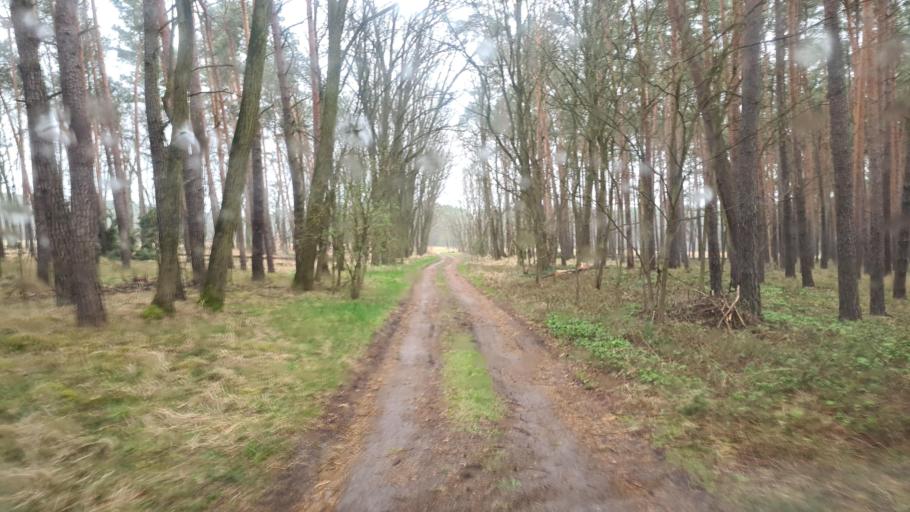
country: DE
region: Brandenburg
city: Bruck
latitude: 52.1626
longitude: 12.7215
